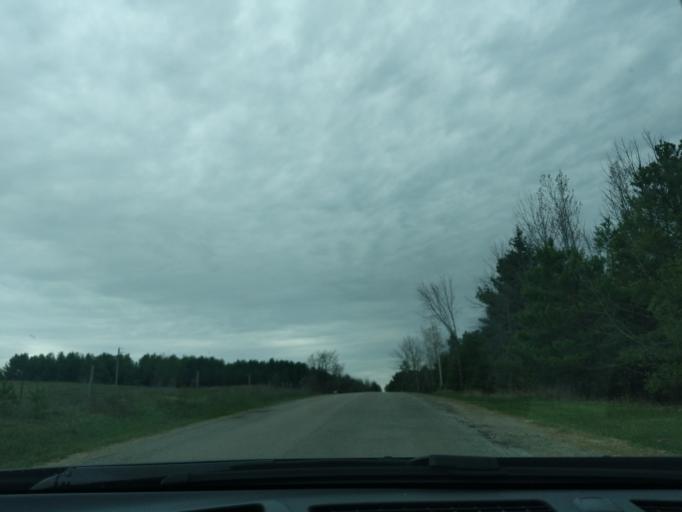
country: CA
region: Ontario
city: Orangeville
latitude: 44.0071
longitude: -79.9654
